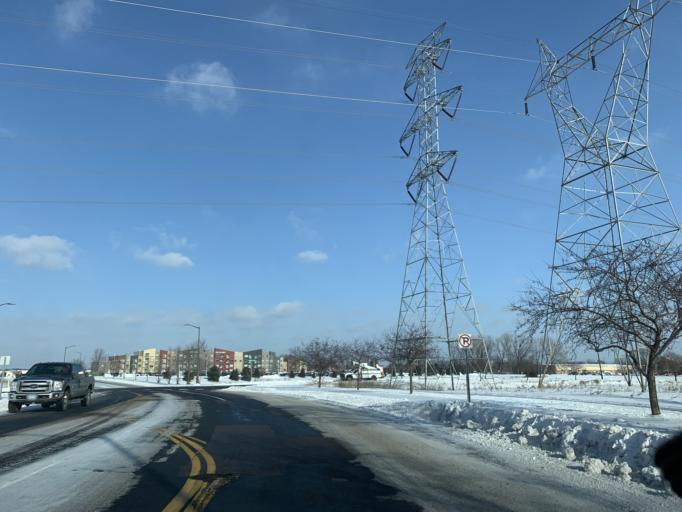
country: US
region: Minnesota
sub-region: Scott County
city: Prior Lake
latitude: 44.7769
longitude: -93.4092
